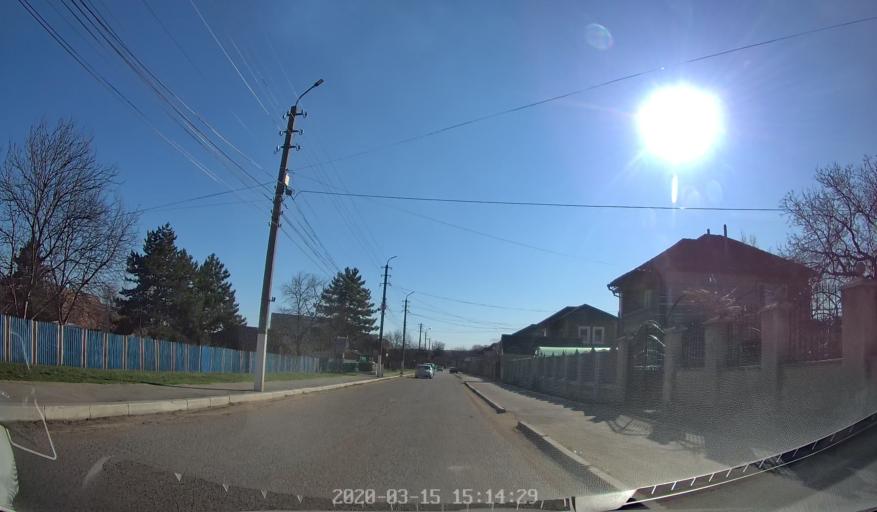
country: MD
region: Chisinau
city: Cricova
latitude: 47.2464
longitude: 28.7667
